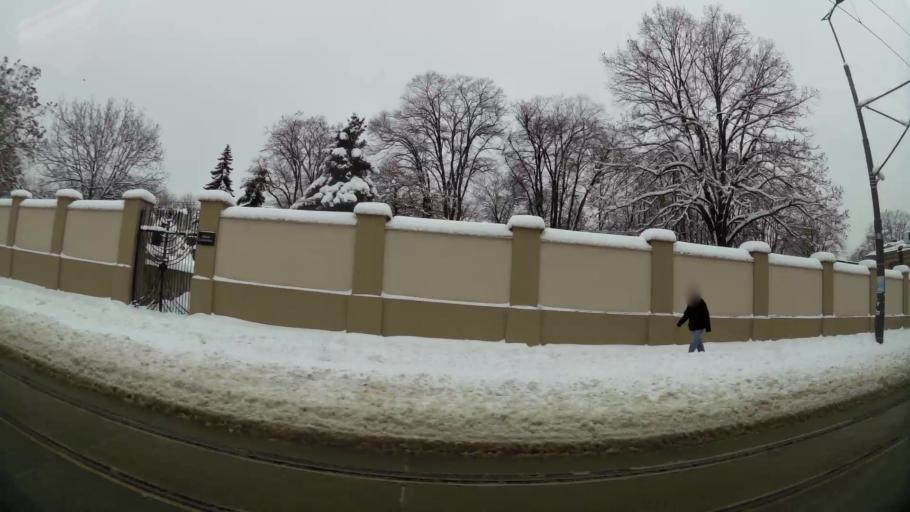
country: RS
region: Central Serbia
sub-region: Belgrade
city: Vracar
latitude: 44.8110
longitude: 20.4870
